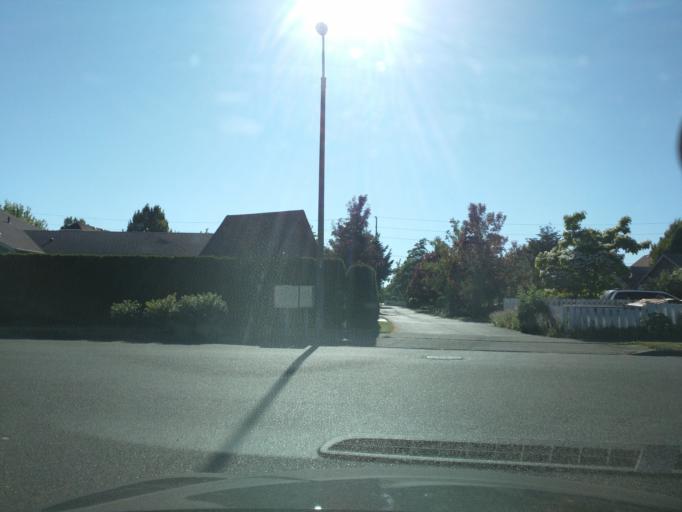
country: US
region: Washington
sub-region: Whatcom County
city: Lynden
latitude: 48.9610
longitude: -122.4282
